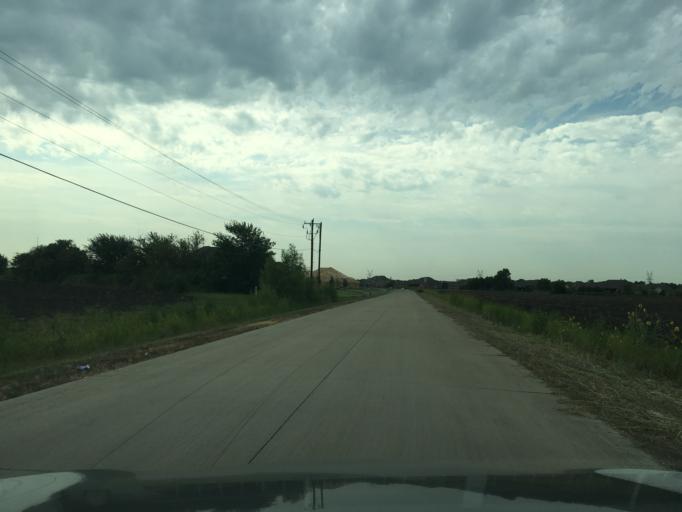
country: US
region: Texas
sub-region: Collin County
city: Parker
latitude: 33.0687
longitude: -96.6087
